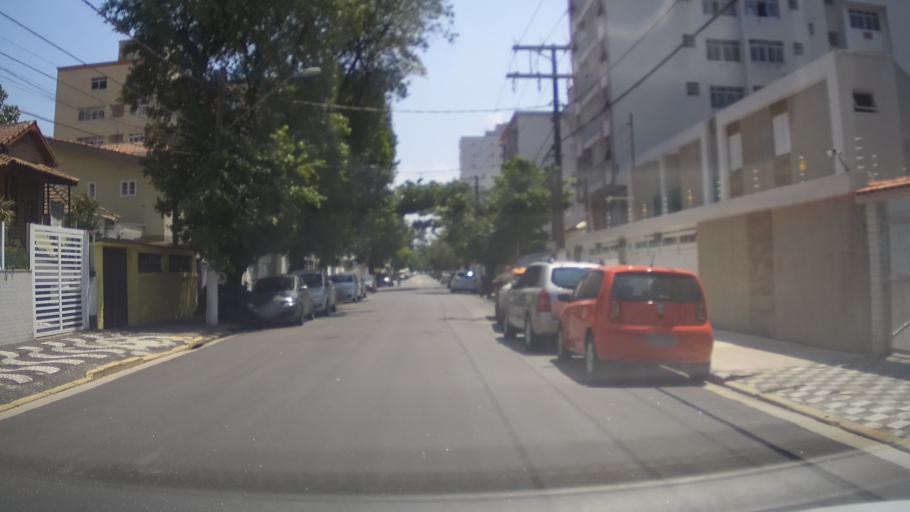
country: BR
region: Sao Paulo
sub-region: Santos
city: Santos
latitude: -23.9720
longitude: -46.3028
